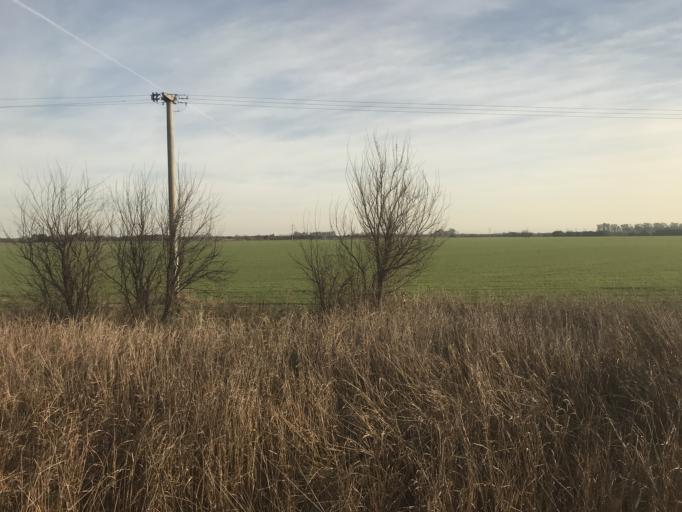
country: AR
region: Cordoba
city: Malvinas Argentinas
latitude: -31.4706
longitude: -64.0975
